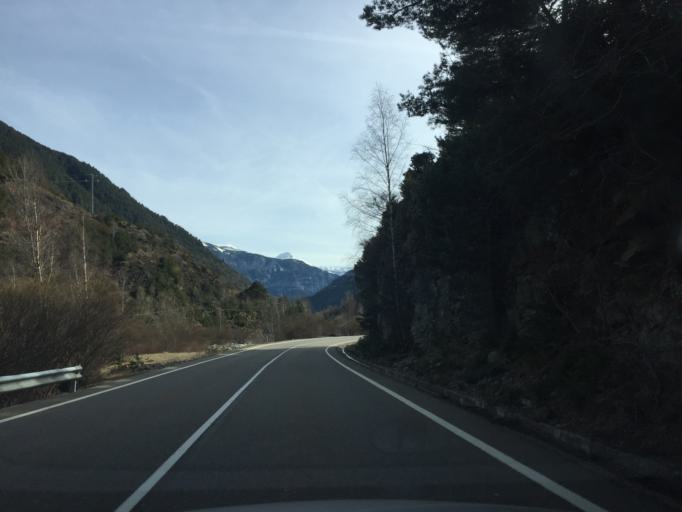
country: ES
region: Aragon
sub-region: Provincia de Huesca
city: Bielsa
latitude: 42.6511
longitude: 0.2091
